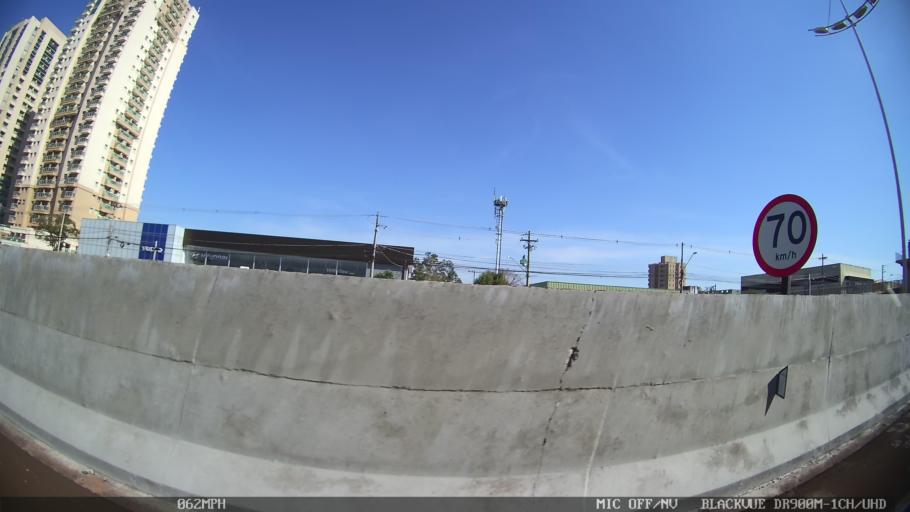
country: BR
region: Sao Paulo
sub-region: Ribeirao Preto
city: Ribeirao Preto
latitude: -21.1974
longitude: -47.7708
